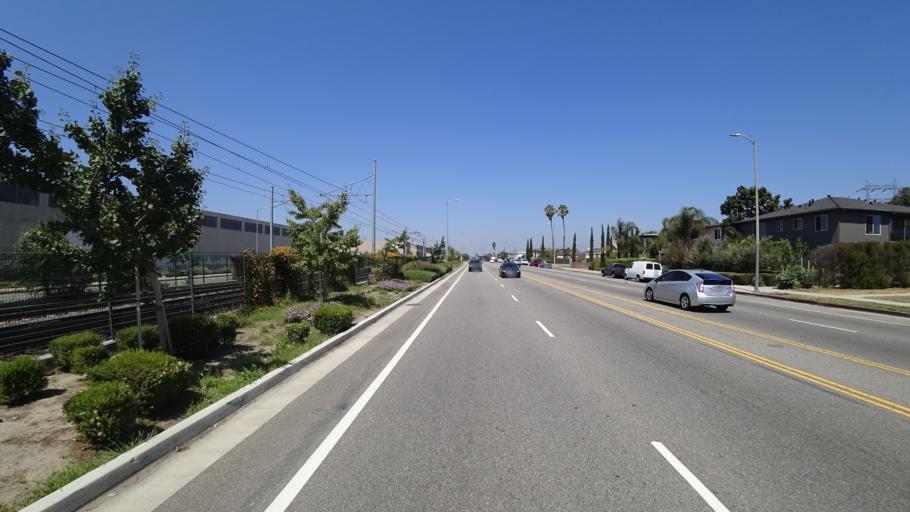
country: US
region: California
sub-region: Los Angeles County
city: Culver City
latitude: 34.0261
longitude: -118.3669
